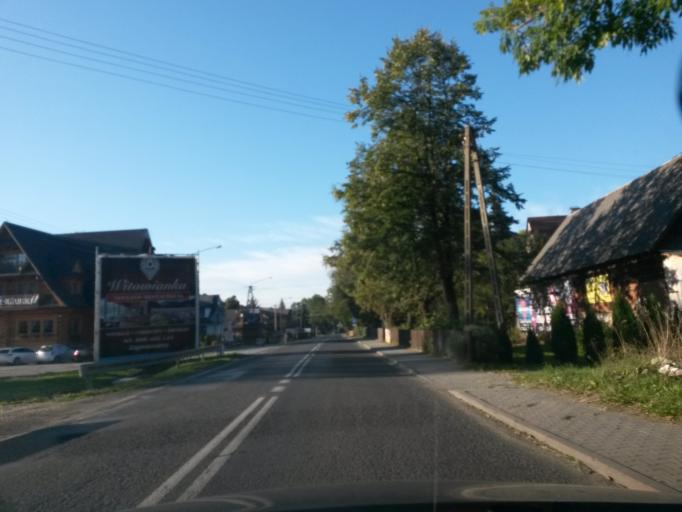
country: PL
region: Lesser Poland Voivodeship
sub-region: Powiat tatrzanski
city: Koscielisko
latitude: 49.3214
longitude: 19.8264
